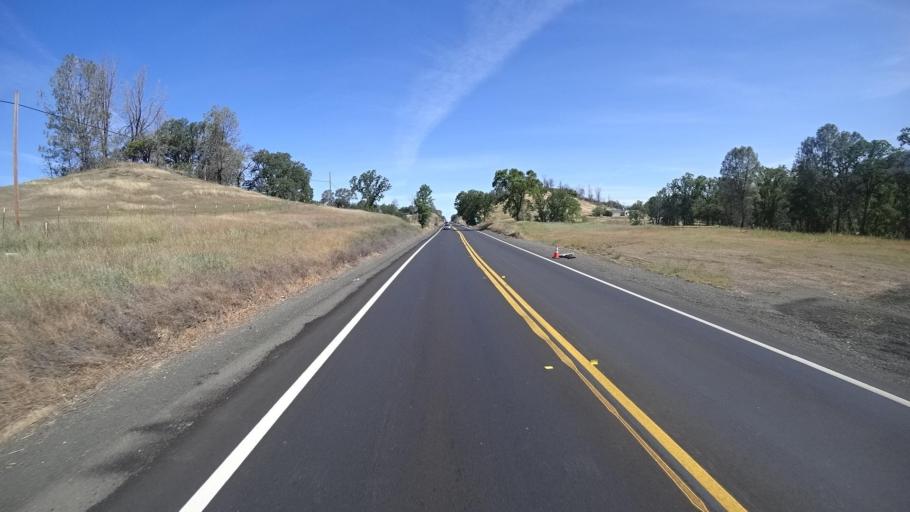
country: US
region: California
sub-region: Lake County
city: Kelseyville
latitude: 38.9503
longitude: -122.8260
